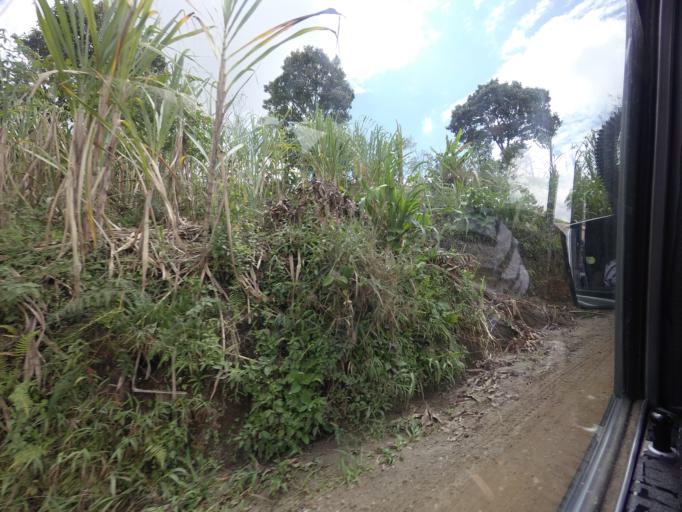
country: CO
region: Huila
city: Isnos
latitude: 1.9404
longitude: -76.2682
